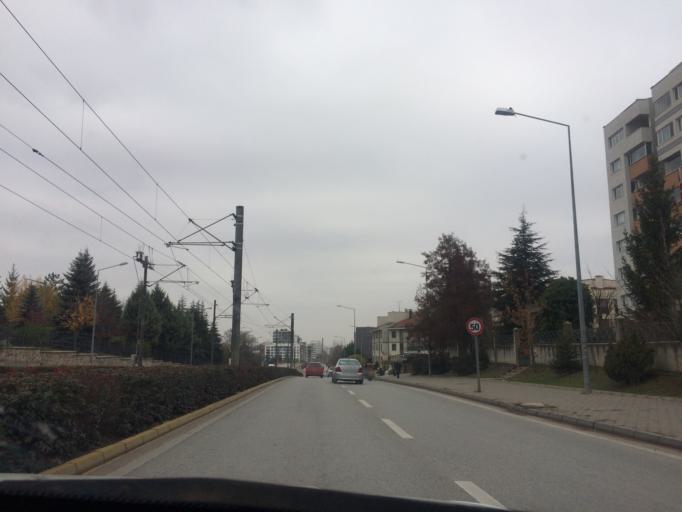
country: TR
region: Eskisehir
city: Eskisehir
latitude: 39.7887
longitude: 30.4930
